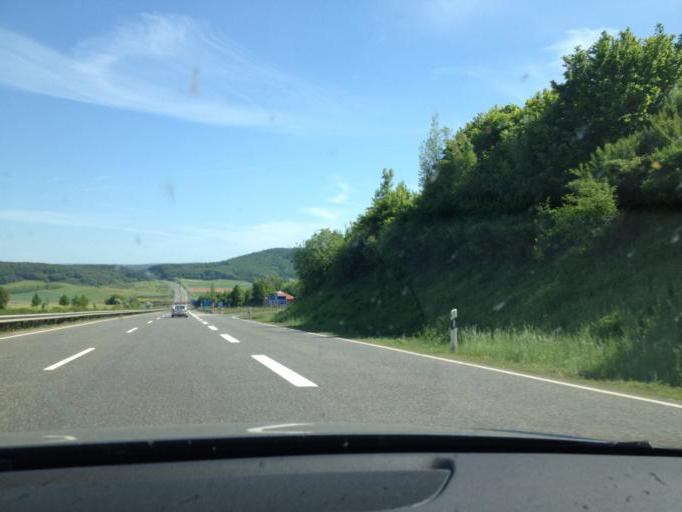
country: DE
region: Rheinland-Pfalz
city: Bergweiler
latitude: 49.9701
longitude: 6.8343
